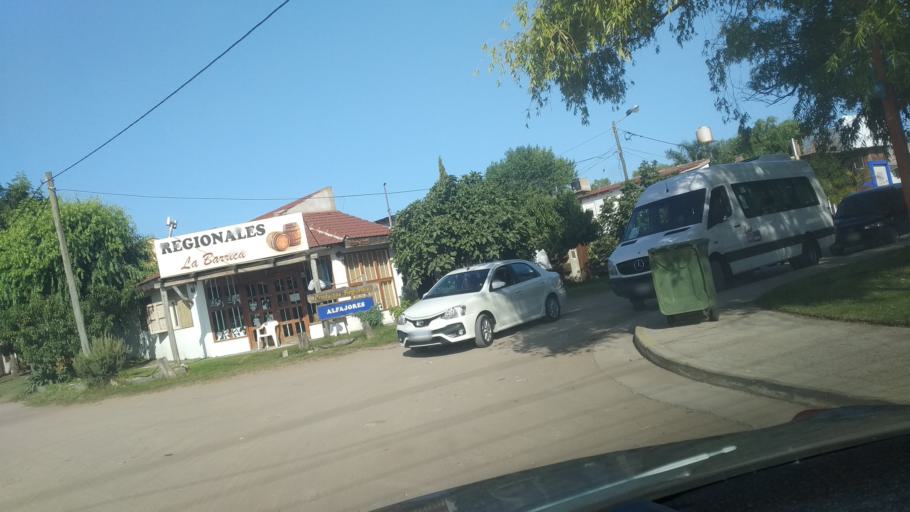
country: AR
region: Buenos Aires
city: Mar del Tuyu
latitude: -36.5325
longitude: -56.7148
